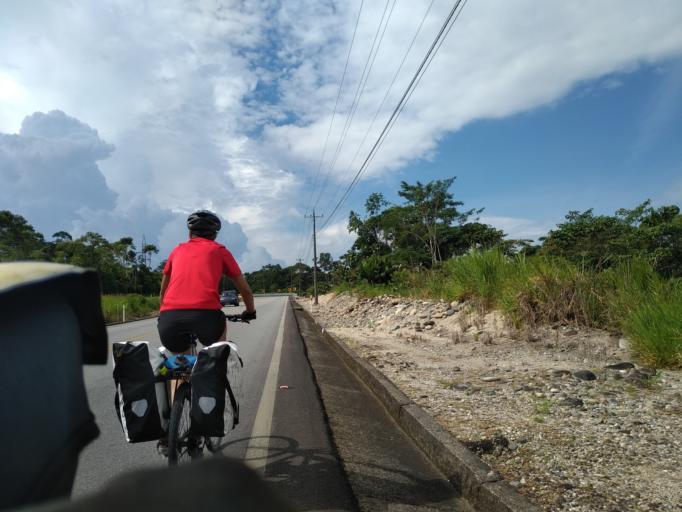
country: EC
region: Napo
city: Tena
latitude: -1.0900
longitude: -77.7898
